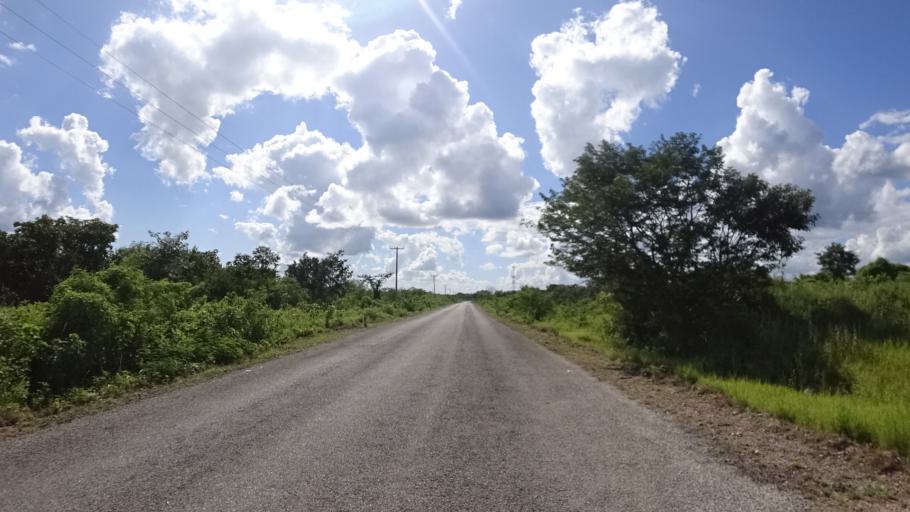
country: MX
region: Yucatan
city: Muna
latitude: 20.6480
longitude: -89.7066
